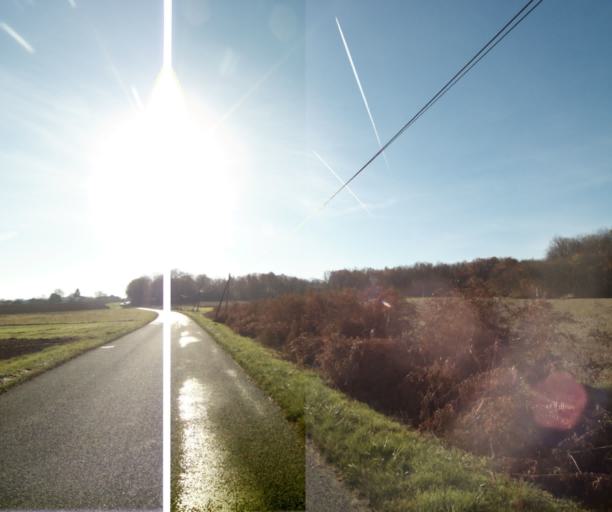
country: FR
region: Poitou-Charentes
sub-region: Departement de la Charente-Maritime
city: Cherac
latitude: 45.7145
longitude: -0.4534
